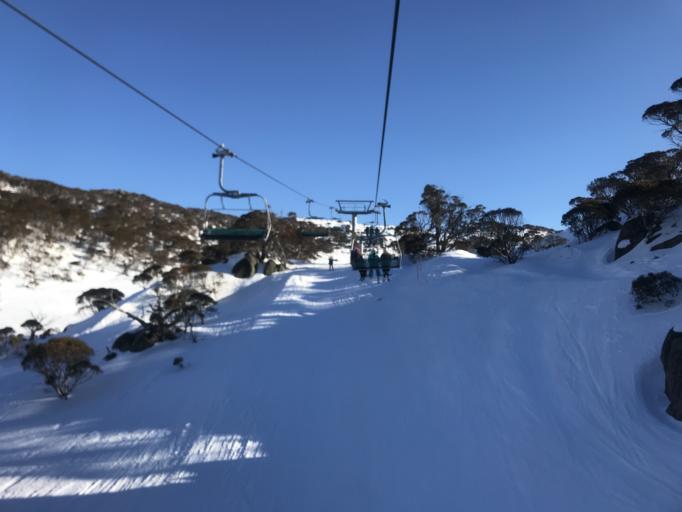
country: AU
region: New South Wales
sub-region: Snowy River
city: Jindabyne
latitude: -36.3881
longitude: 148.3984
